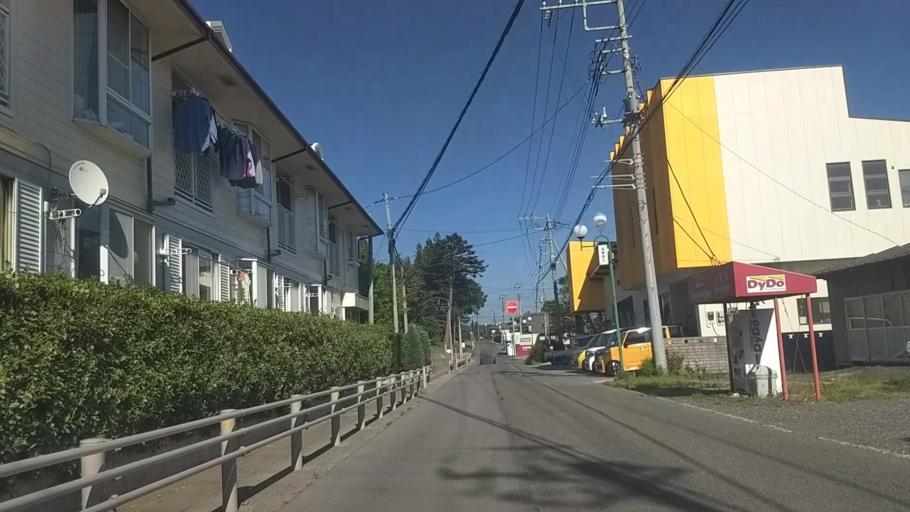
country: JP
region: Nagano
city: Chino
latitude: 35.8623
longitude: 138.3089
